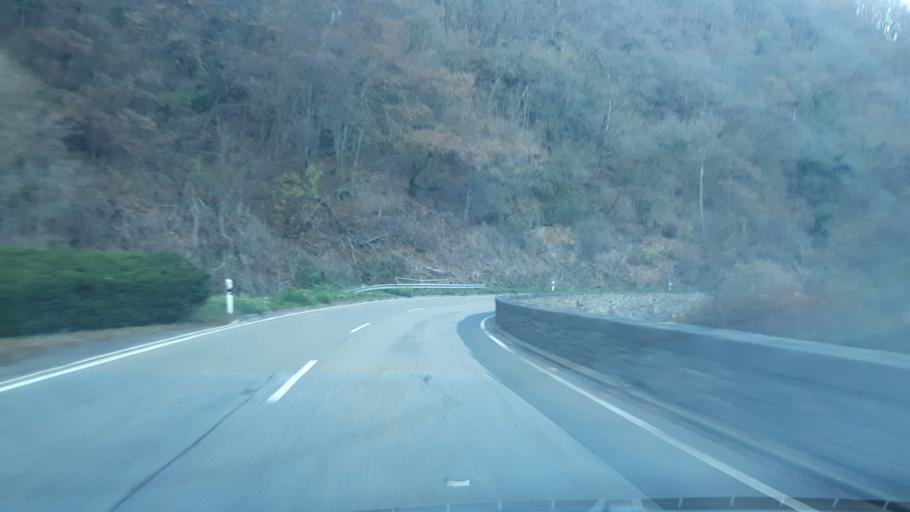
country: DE
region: Rheinland-Pfalz
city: Bad Bertrich
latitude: 50.0698
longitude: 7.0617
